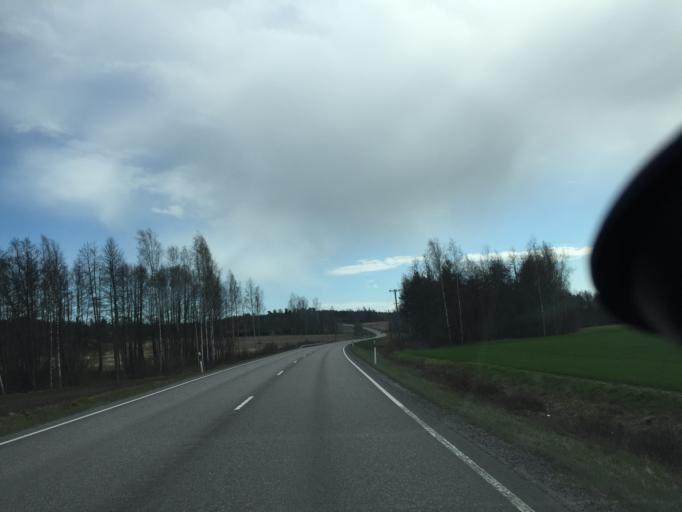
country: FI
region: Uusimaa
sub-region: Raaseporin
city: Ekenaes
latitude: 60.0541
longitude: 23.3301
